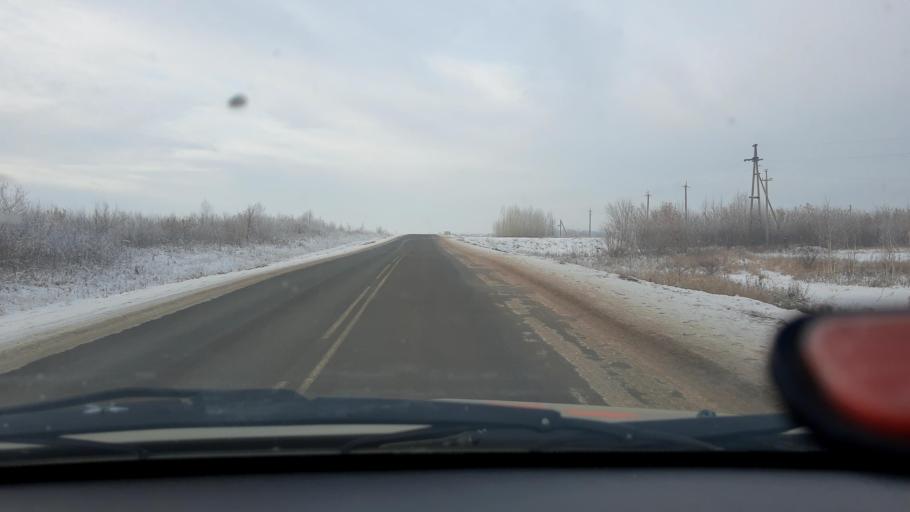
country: RU
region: Bashkortostan
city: Avdon
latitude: 54.3658
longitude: 55.8275
